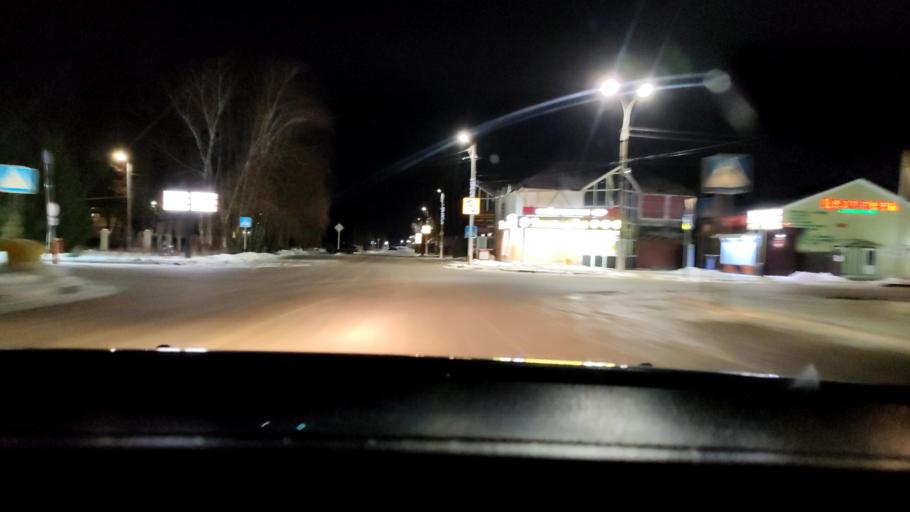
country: RU
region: Voronezj
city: Ramon'
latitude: 51.9136
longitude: 39.3372
